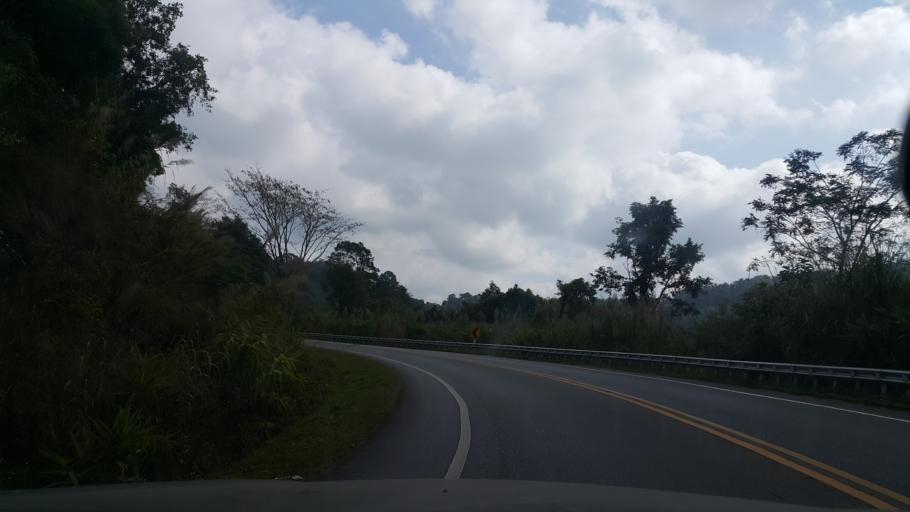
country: TH
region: Phayao
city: Phayao
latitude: 19.0707
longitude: 99.7678
